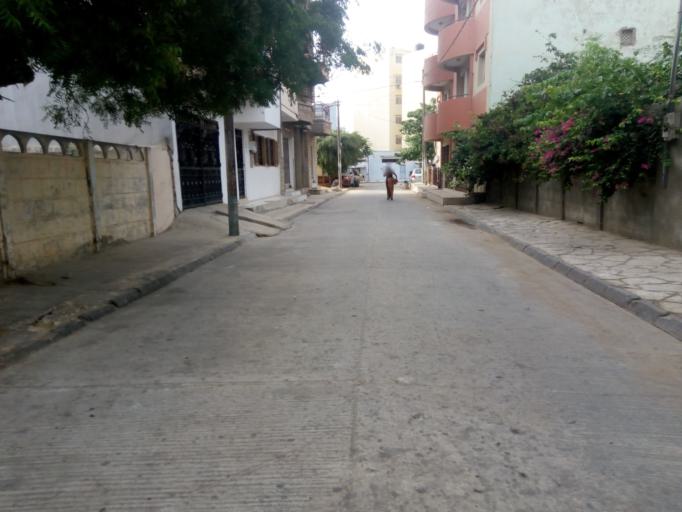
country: SN
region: Dakar
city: Dakar
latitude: 14.6987
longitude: -17.4562
